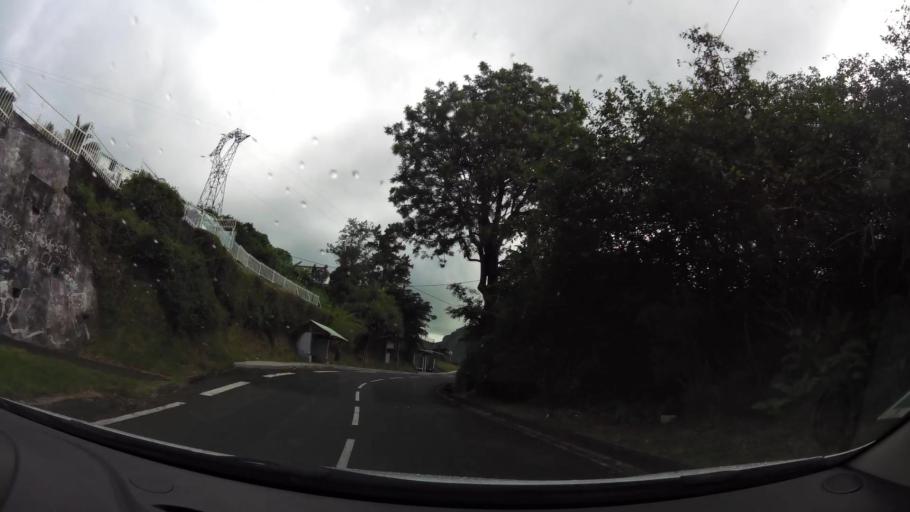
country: RE
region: Reunion
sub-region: Reunion
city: Saint-Denis
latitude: -20.9043
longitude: 55.4417
